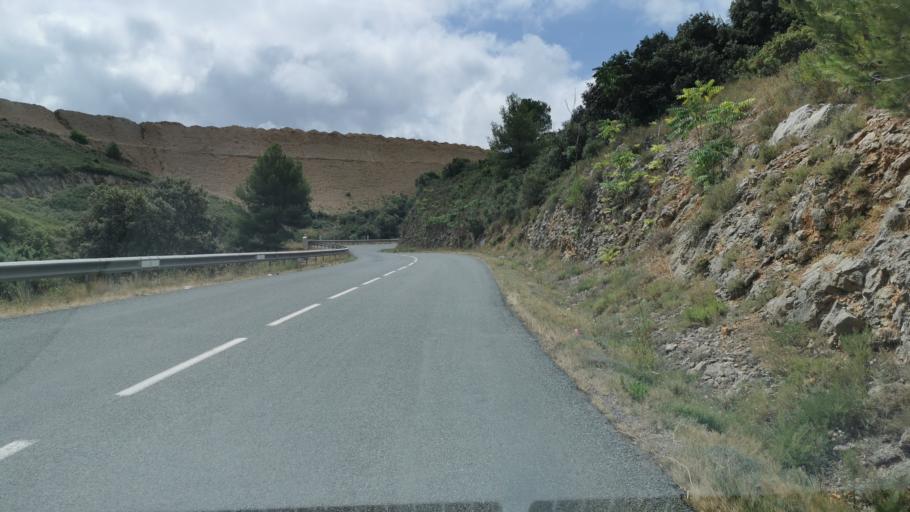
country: FR
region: Languedoc-Roussillon
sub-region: Departement de l'Aude
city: Bizanet
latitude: 43.1675
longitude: 2.9015
